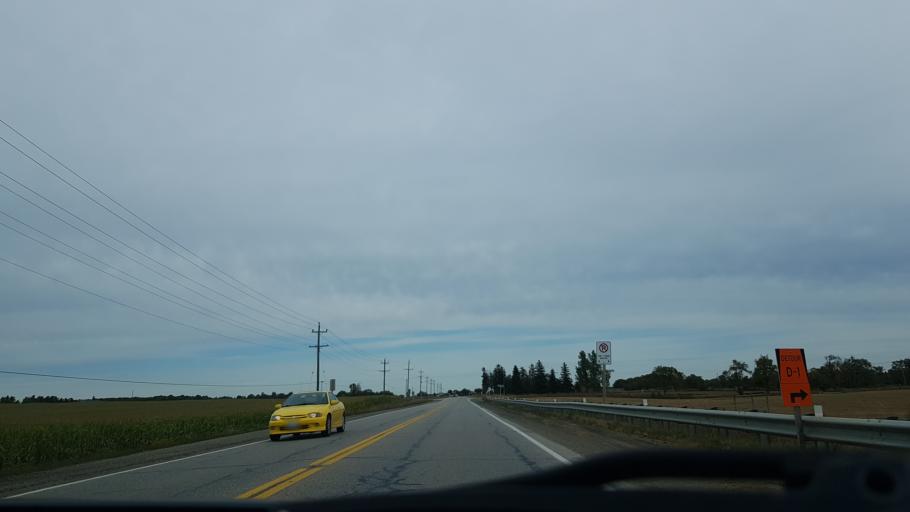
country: CA
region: Ontario
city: Orangeville
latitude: 43.8187
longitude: -80.0417
